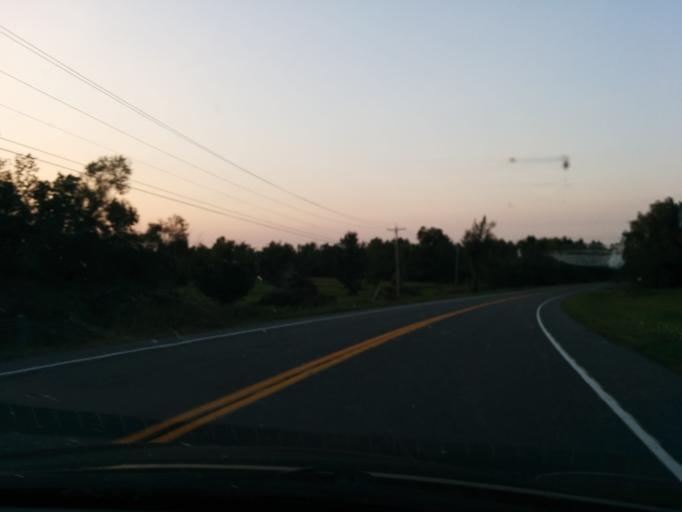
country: US
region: New York
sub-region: Jefferson County
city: Alexandria Bay
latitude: 44.2770
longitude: -75.8077
